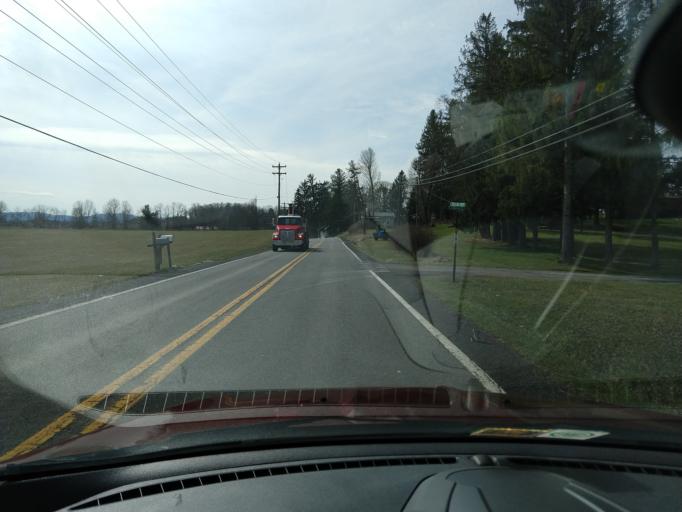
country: US
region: West Virginia
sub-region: Greenbrier County
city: Lewisburg
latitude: 37.8800
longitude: -80.4121
